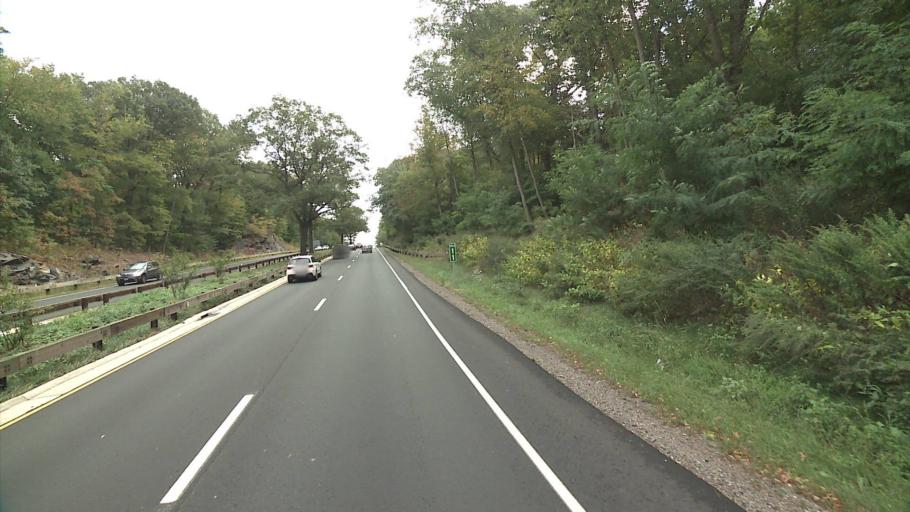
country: US
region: Connecticut
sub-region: Fairfield County
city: North Stamford
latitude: 41.1141
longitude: -73.5406
